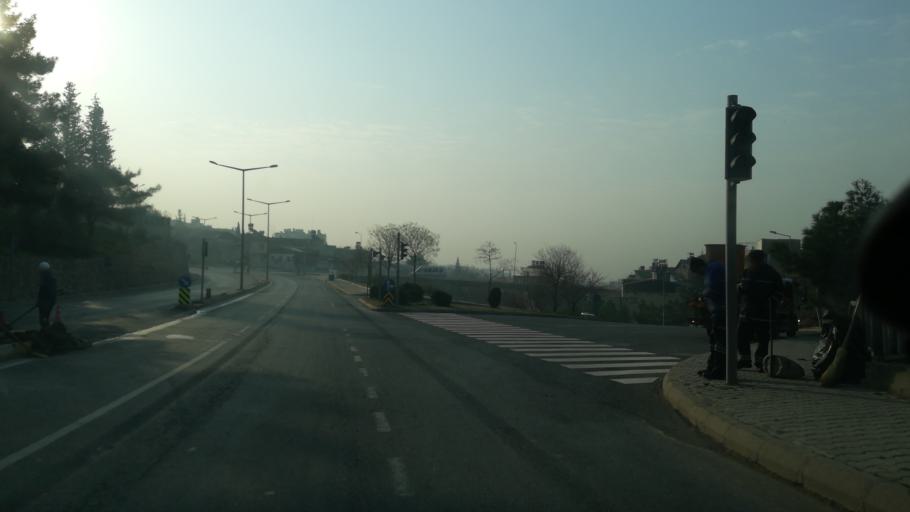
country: TR
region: Kahramanmaras
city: Kahramanmaras
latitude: 37.5935
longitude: 36.9259
